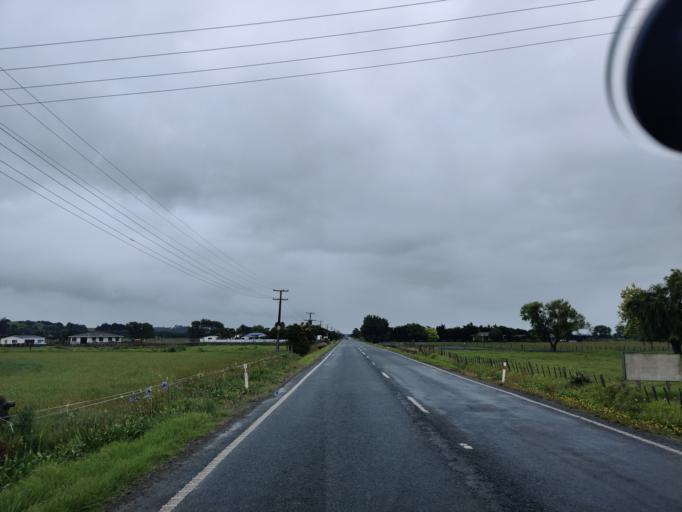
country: NZ
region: Northland
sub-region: Kaipara District
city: Dargaville
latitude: -35.9455
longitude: 173.8884
